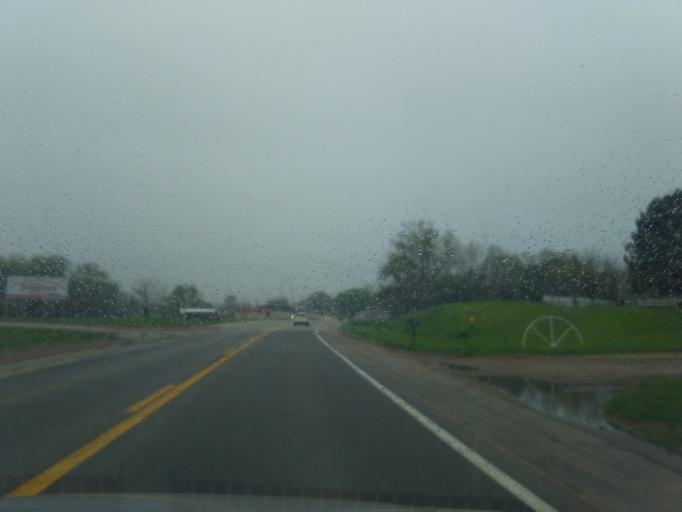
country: US
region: Nebraska
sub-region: Cuming County
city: Wisner
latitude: 41.9818
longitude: -96.9062
